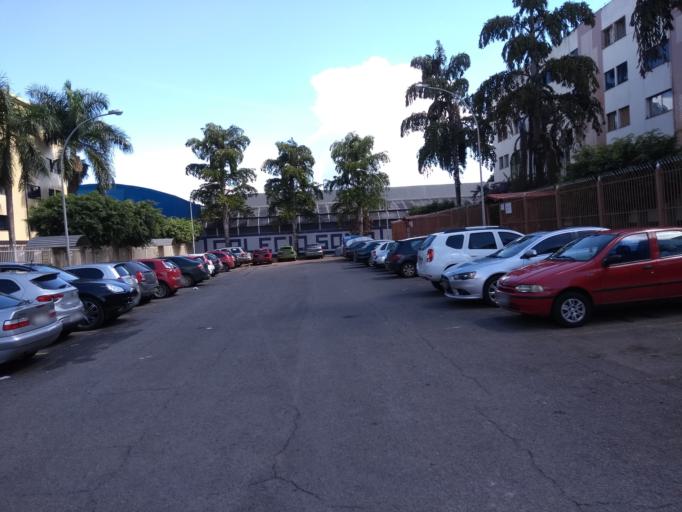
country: BR
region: Federal District
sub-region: Brasilia
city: Brasilia
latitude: -15.7940
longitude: -47.9394
